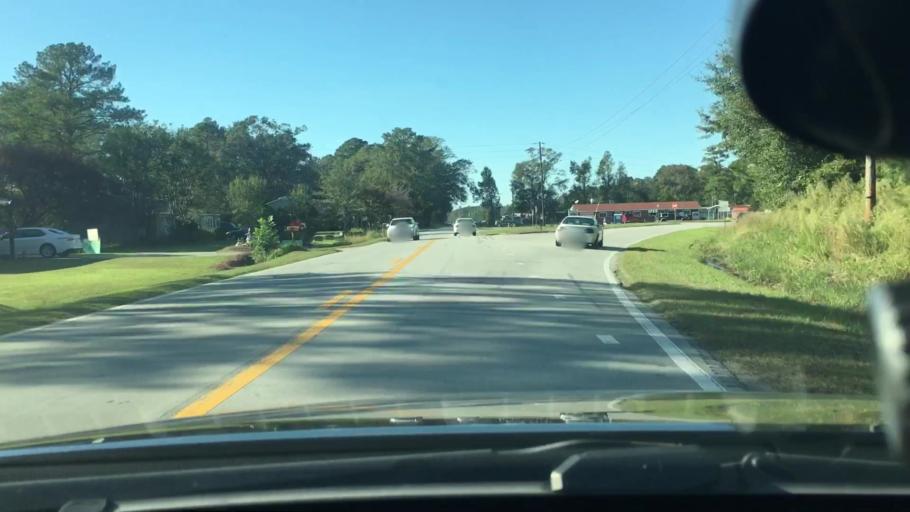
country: US
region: North Carolina
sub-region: Craven County
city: Vanceboro
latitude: 35.2289
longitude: -77.1357
